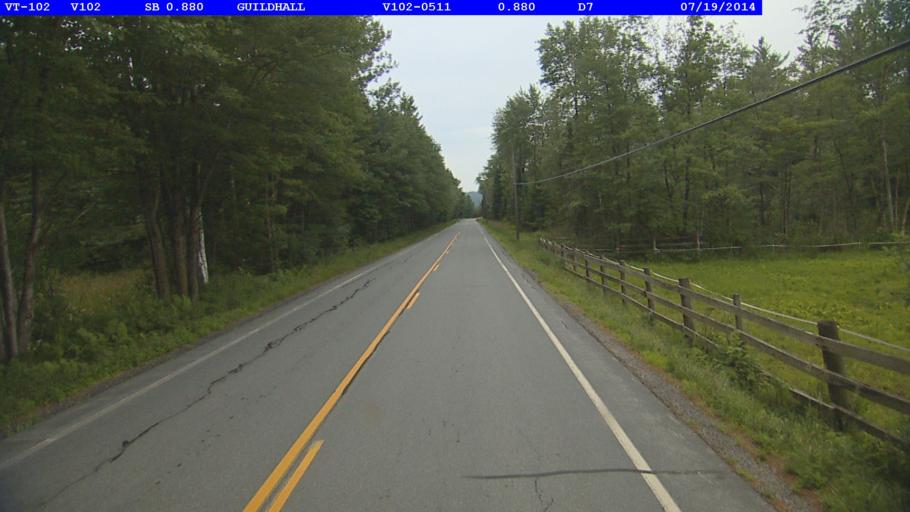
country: US
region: New Hampshire
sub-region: Coos County
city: Lancaster
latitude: 44.5080
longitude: -71.5938
